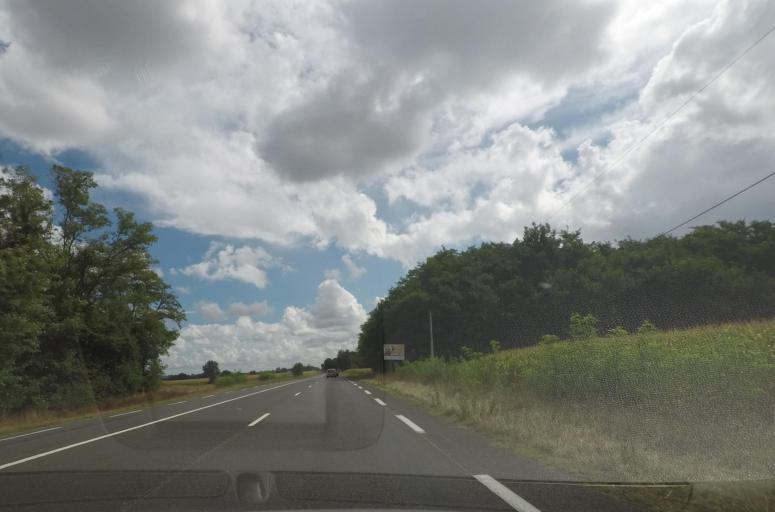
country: FR
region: Pays de la Loire
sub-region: Departement de la Sarthe
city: Bazouges-sur-le-Loir
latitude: 47.6925
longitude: -0.1355
